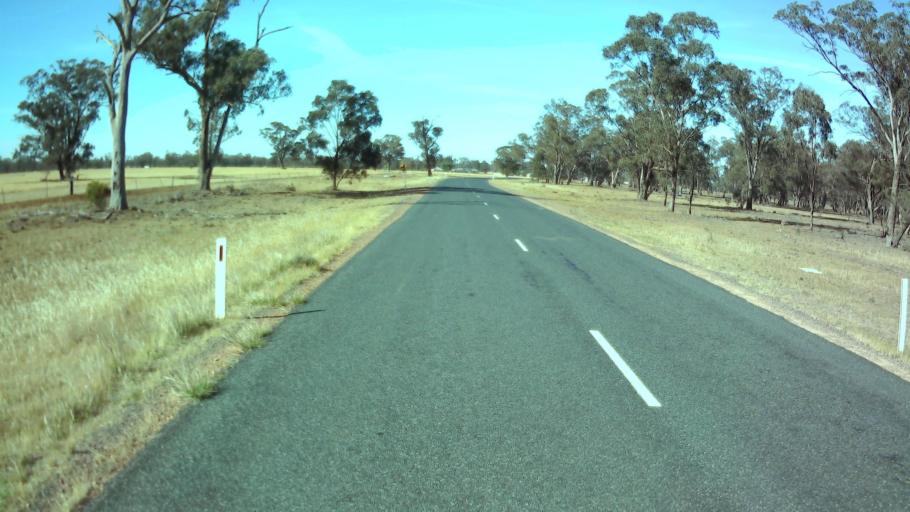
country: AU
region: New South Wales
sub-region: Weddin
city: Grenfell
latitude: -34.0942
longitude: 147.8867
